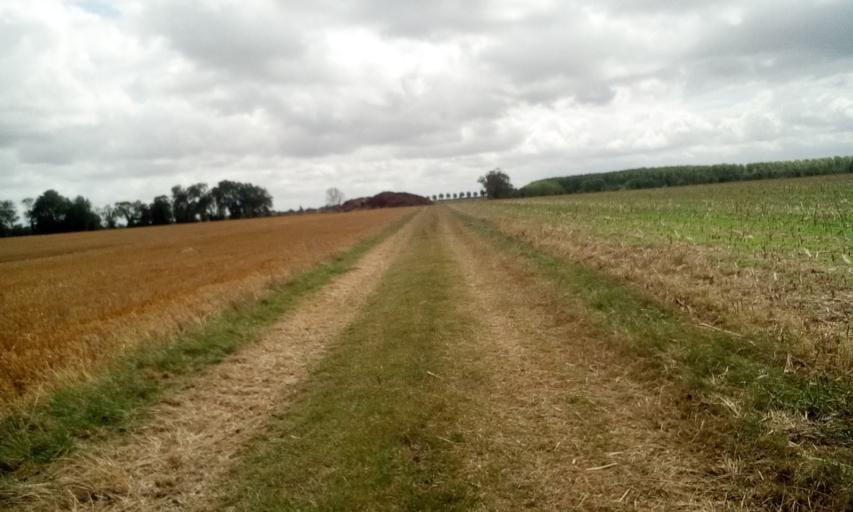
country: FR
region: Lower Normandy
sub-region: Departement du Calvados
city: Cheux
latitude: 49.1901
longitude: -0.5319
